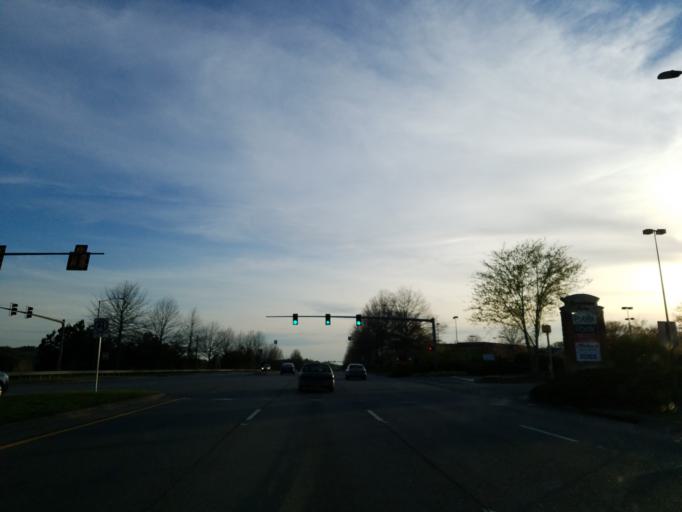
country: US
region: Georgia
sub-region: Cherokee County
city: Canton
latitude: 34.2506
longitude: -84.4747
